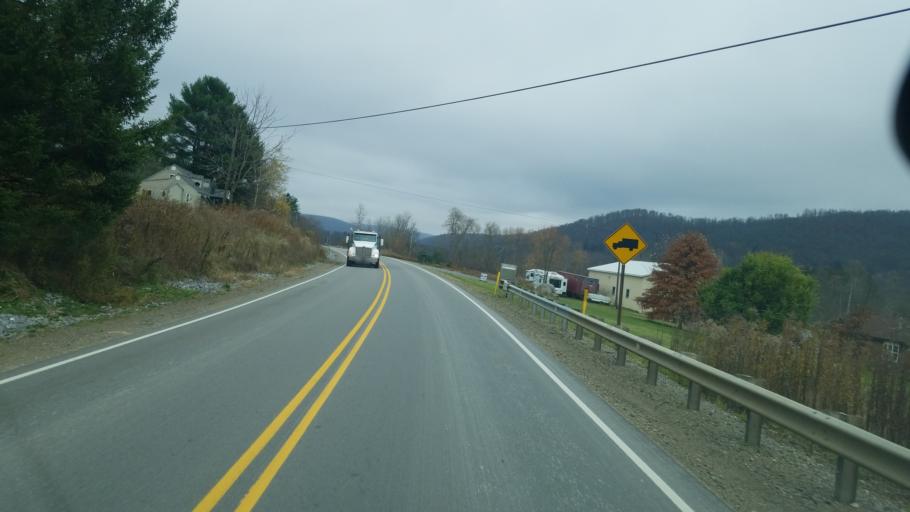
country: US
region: Pennsylvania
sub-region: McKean County
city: Smethport
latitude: 41.7861
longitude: -78.4143
